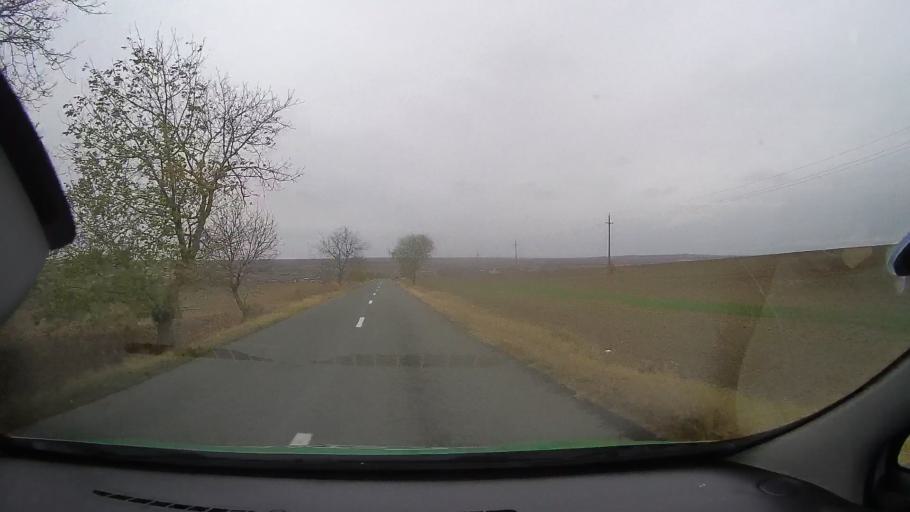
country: RO
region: Constanta
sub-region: Comuna Targusor
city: Targusor
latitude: 44.4853
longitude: 28.3676
